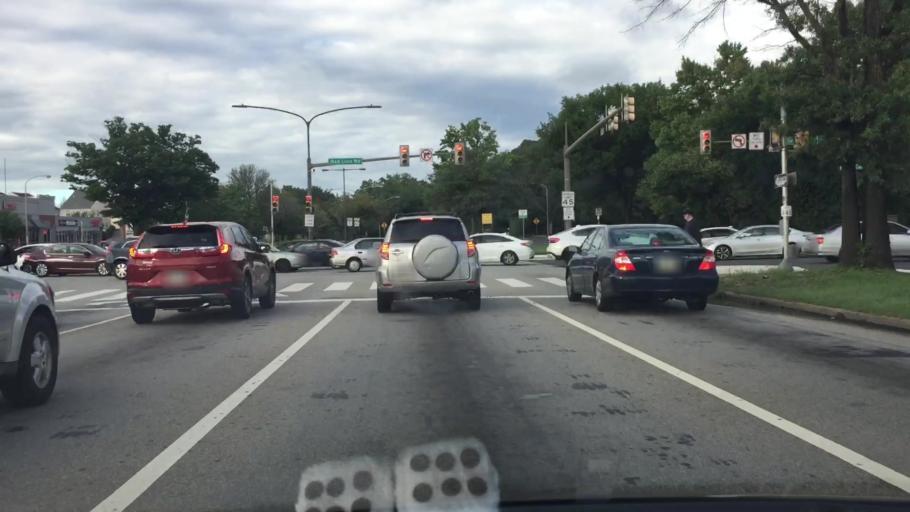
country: US
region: Pennsylvania
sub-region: Bucks County
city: Feasterville
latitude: 40.0944
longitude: -75.0155
